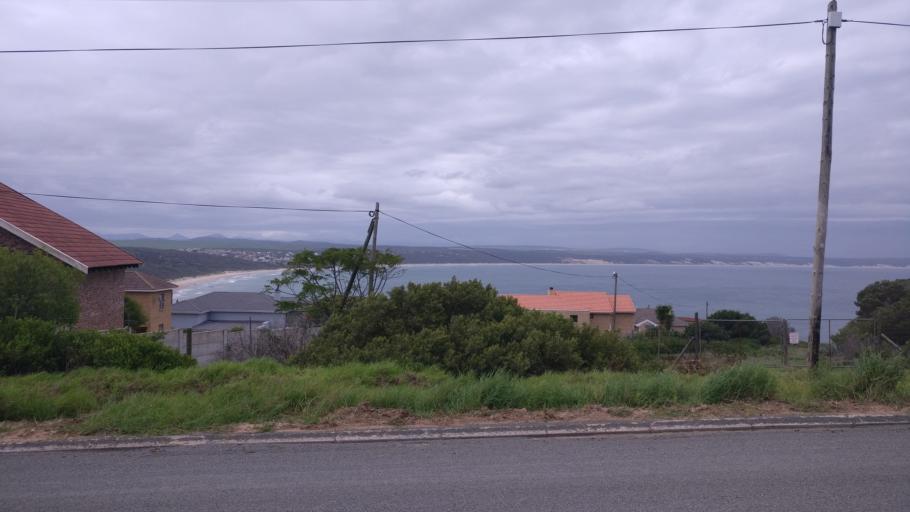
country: ZA
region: Western Cape
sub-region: Eden District Municipality
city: Mossel Bay
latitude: -34.2949
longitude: 21.9150
